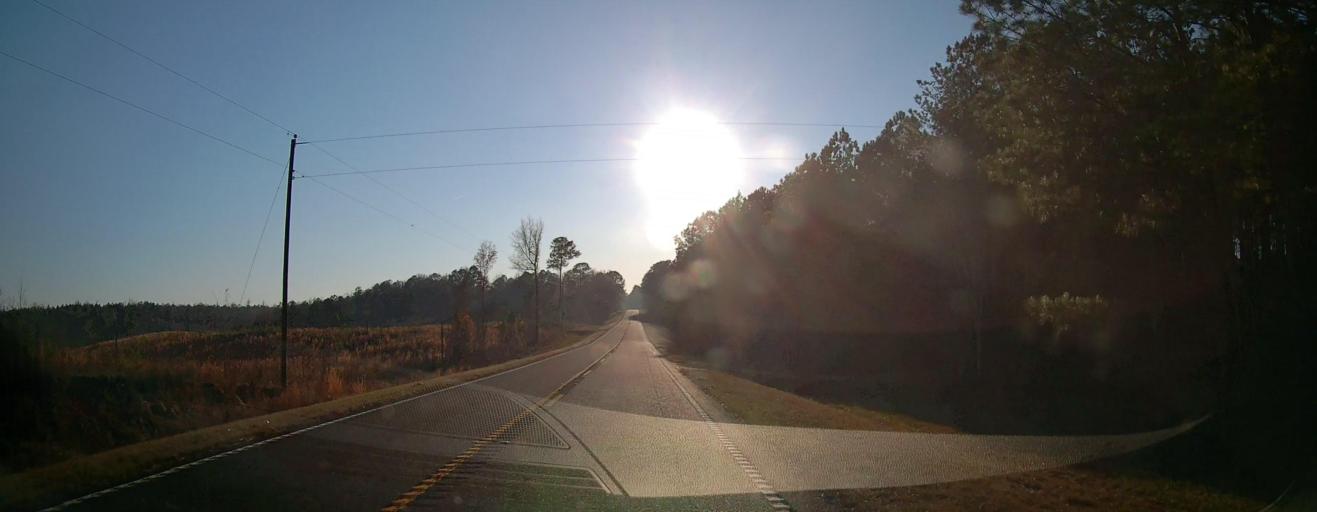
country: US
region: Georgia
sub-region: Talbot County
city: Talbotton
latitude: 32.6646
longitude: -84.6226
